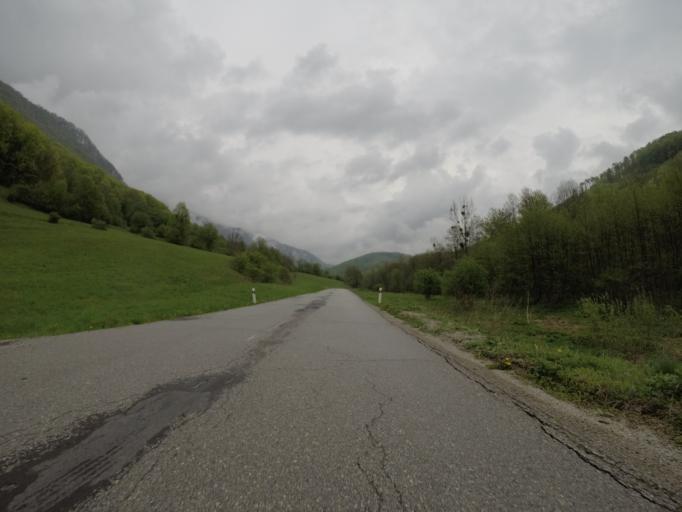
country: SK
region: Banskobystricky
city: Revuca
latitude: 48.7478
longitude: 20.0613
